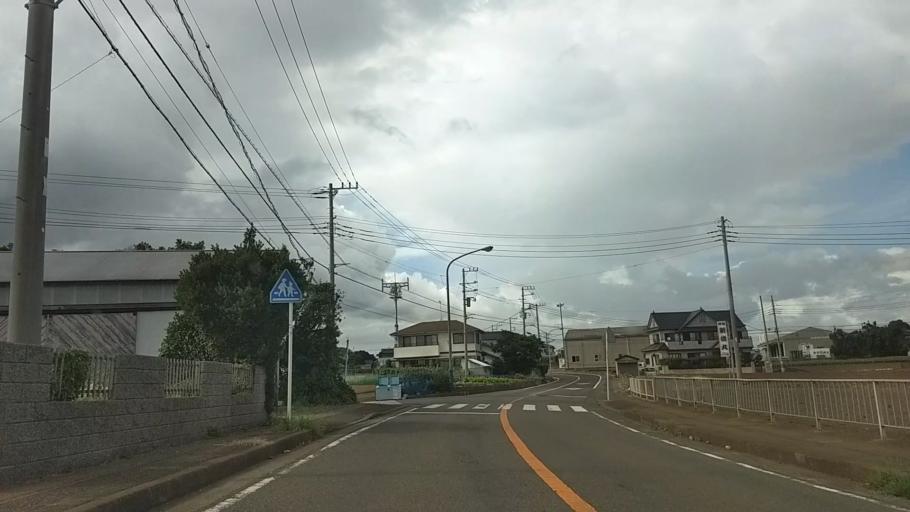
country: JP
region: Kanagawa
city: Miura
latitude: 35.1492
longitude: 139.6686
